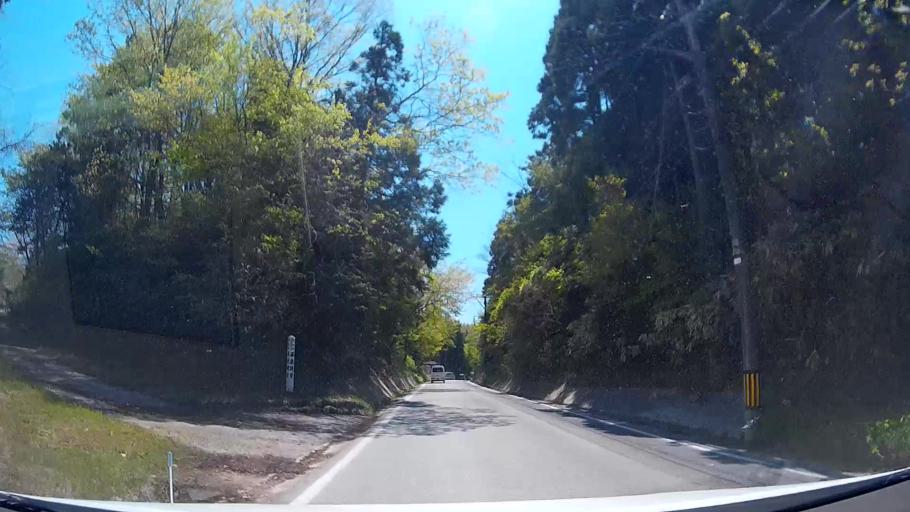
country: JP
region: Ishikawa
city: Nanao
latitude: 37.4551
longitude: 137.3021
